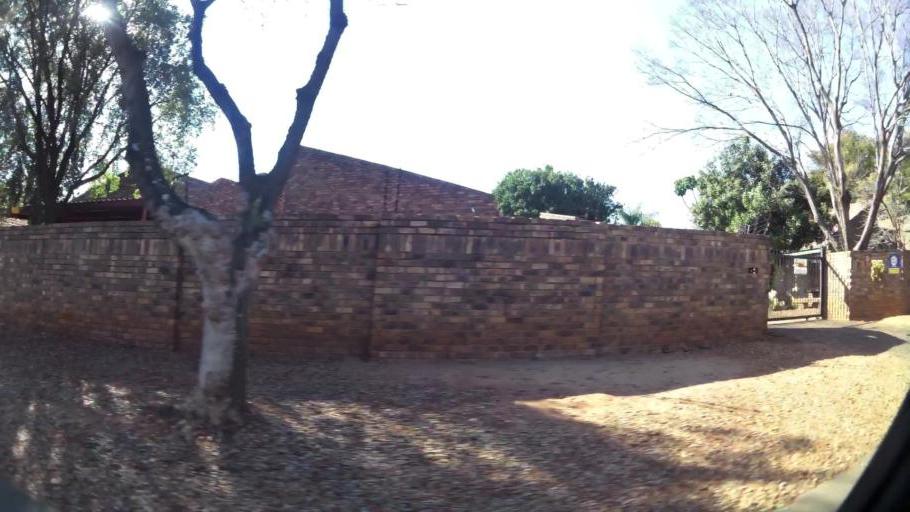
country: ZA
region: Gauteng
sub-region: City of Tshwane Metropolitan Municipality
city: Pretoria
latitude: -25.6796
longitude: 28.1436
